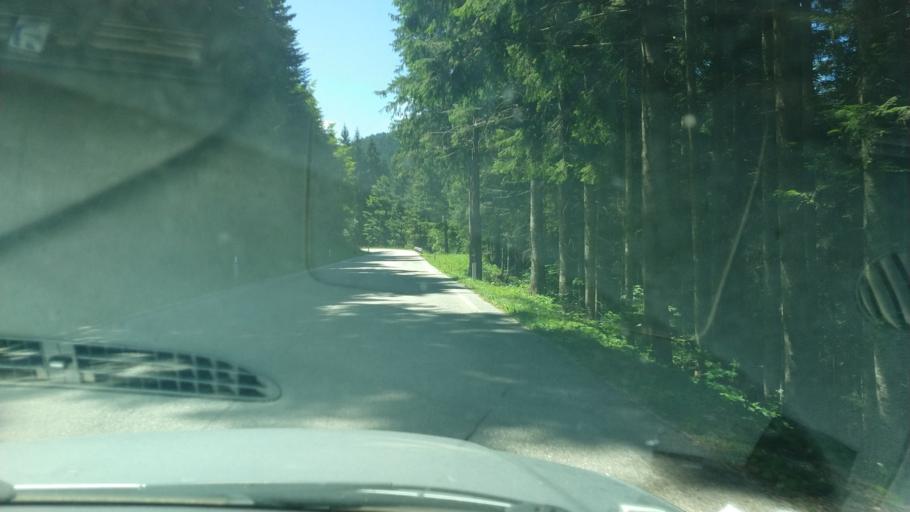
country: IT
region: Trentino-Alto Adige
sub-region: Provincia di Trento
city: Folgaria
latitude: 45.9034
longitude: 11.2127
